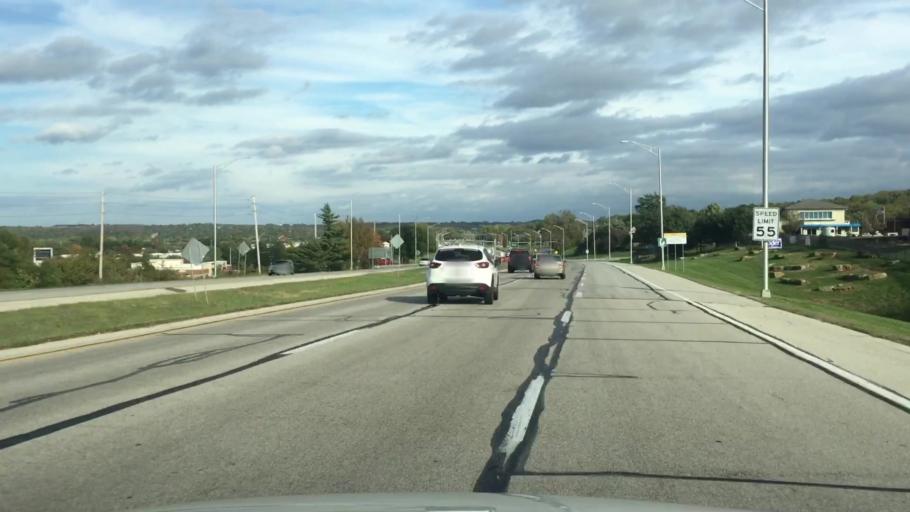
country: US
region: Kansas
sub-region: Wyandotte County
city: Edwardsville
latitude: 39.0071
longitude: -94.8487
